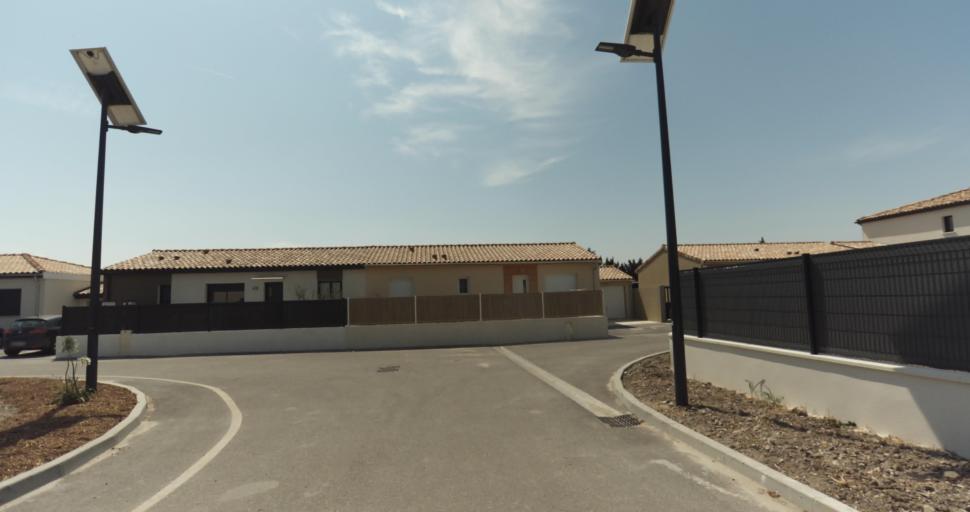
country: FR
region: Provence-Alpes-Cote d'Azur
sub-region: Departement du Vaucluse
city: Monteux
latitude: 44.0305
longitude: 4.9811
